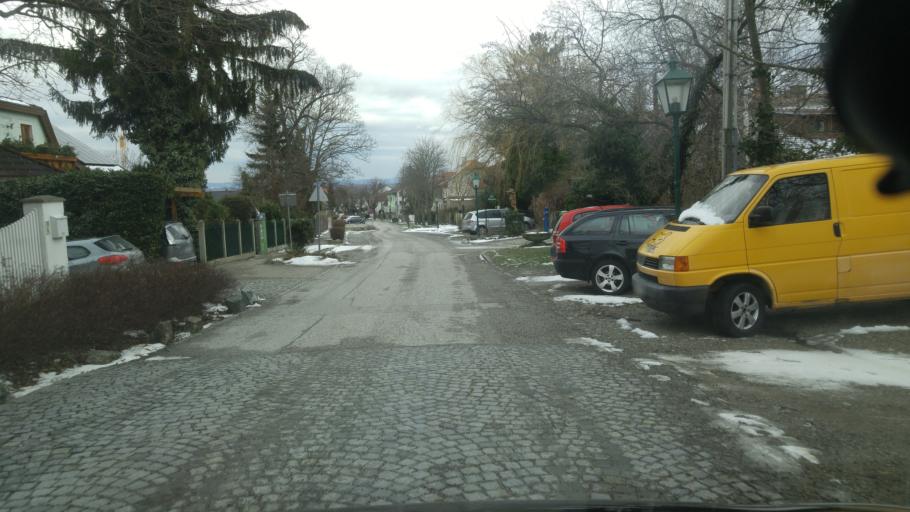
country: AT
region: Lower Austria
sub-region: Politischer Bezirk Baden
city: Bad Voslau
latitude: 47.9856
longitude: 16.2024
